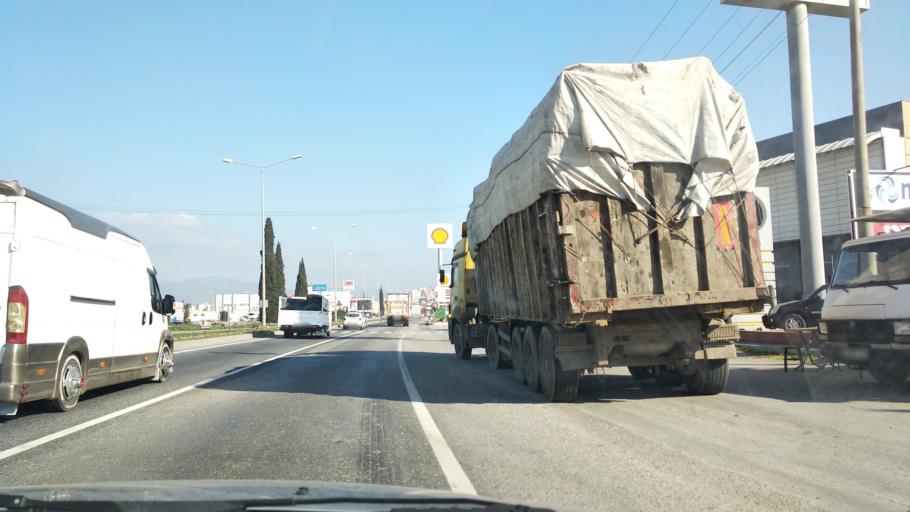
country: TR
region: Izmir
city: Menemen
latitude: 38.5788
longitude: 27.0652
